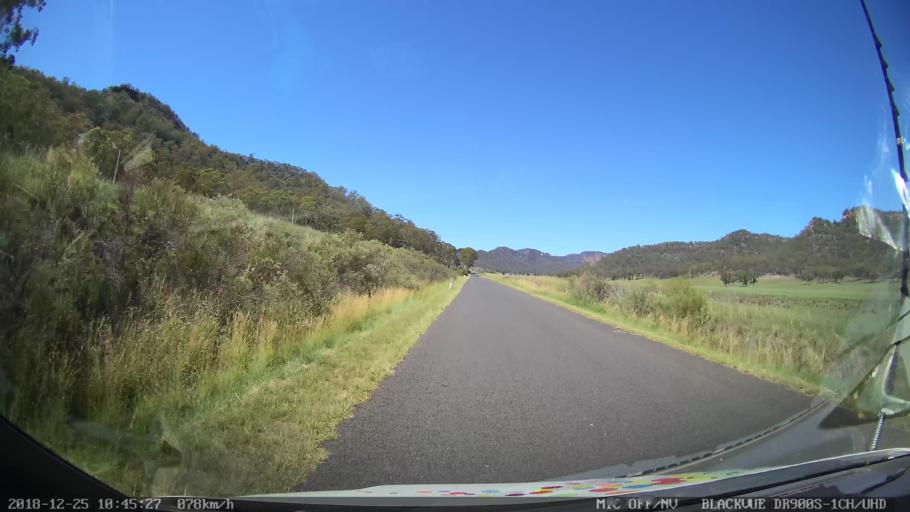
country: AU
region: New South Wales
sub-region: Upper Hunter Shire
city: Merriwa
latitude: -32.4332
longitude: 150.2899
